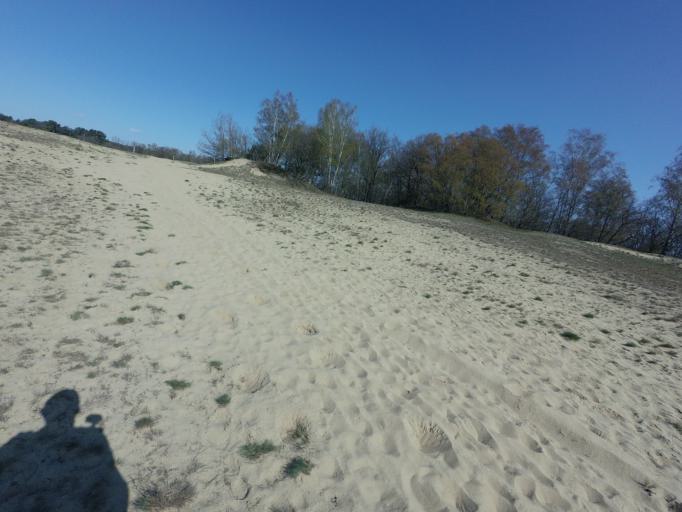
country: NL
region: Limburg
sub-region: Gemeente Bergen
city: Wellerlooi
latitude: 51.6014
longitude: 6.0701
